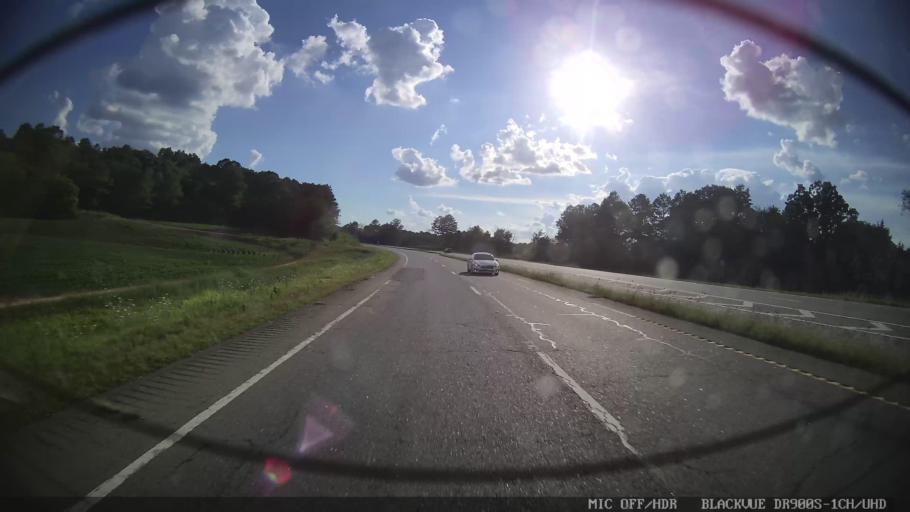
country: US
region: Georgia
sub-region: Bartow County
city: Euharlee
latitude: 34.2074
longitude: -84.9885
